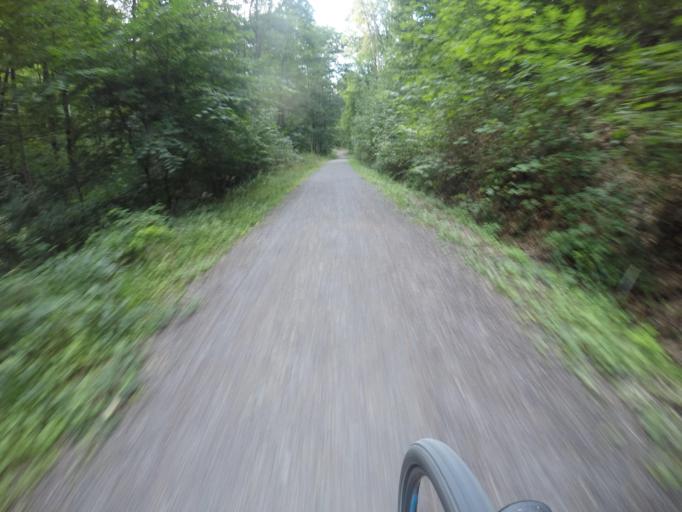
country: DE
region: Baden-Wuerttemberg
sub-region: Regierungsbezirk Stuttgart
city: Ostfildern
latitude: 48.7474
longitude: 9.2472
